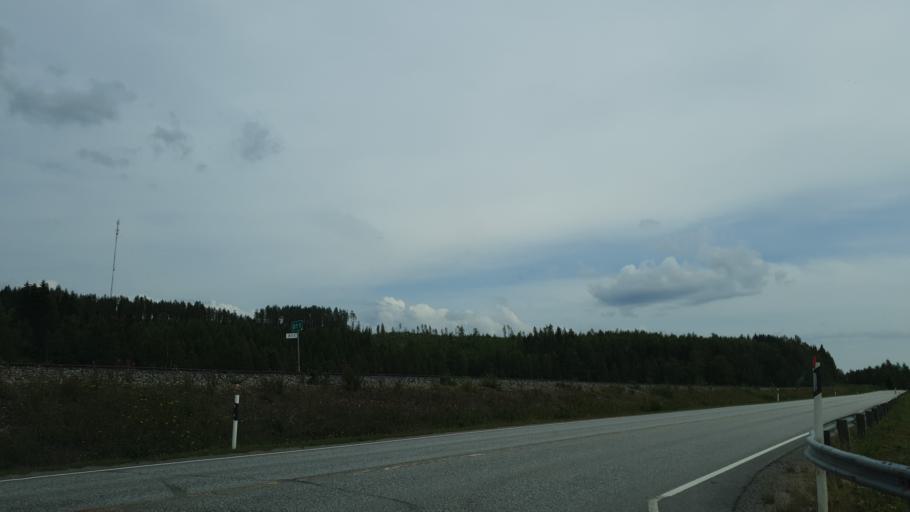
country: FI
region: North Karelia
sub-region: Pielisen Karjala
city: Valtimo
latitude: 63.7022
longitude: 28.7686
